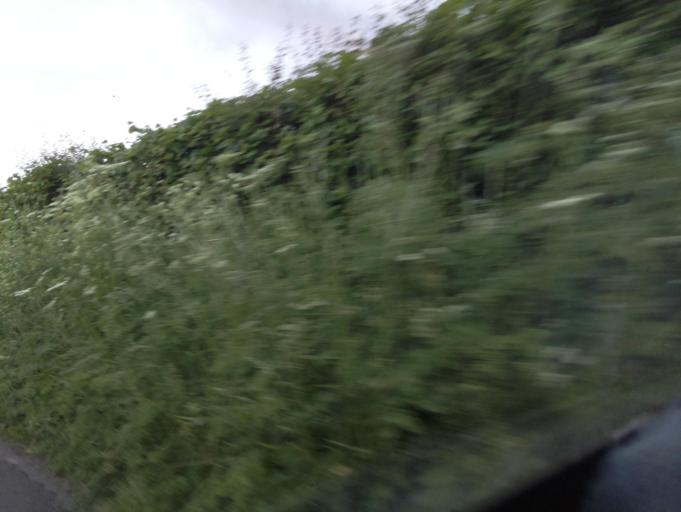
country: GB
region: England
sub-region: South Gloucestershire
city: Pucklechurch
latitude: 51.4667
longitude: -2.4246
